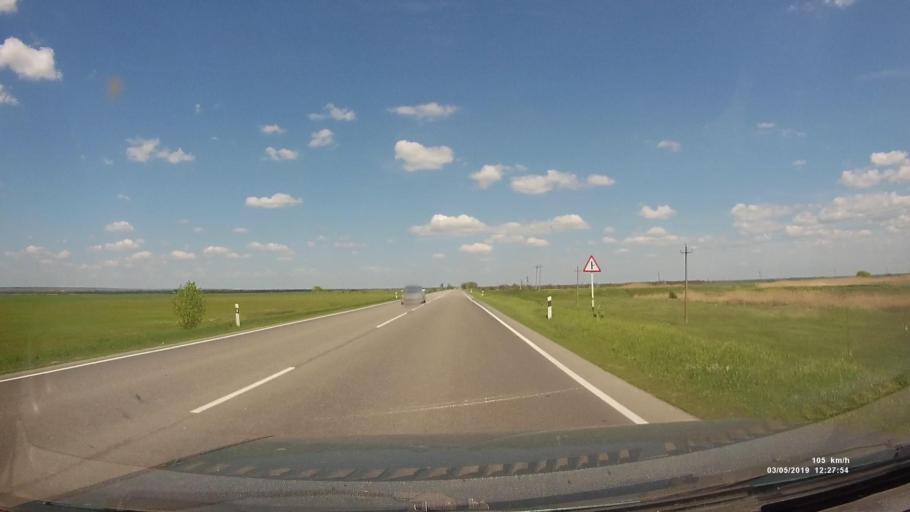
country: RU
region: Rostov
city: Semikarakorsk
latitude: 47.4653
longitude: 40.7241
